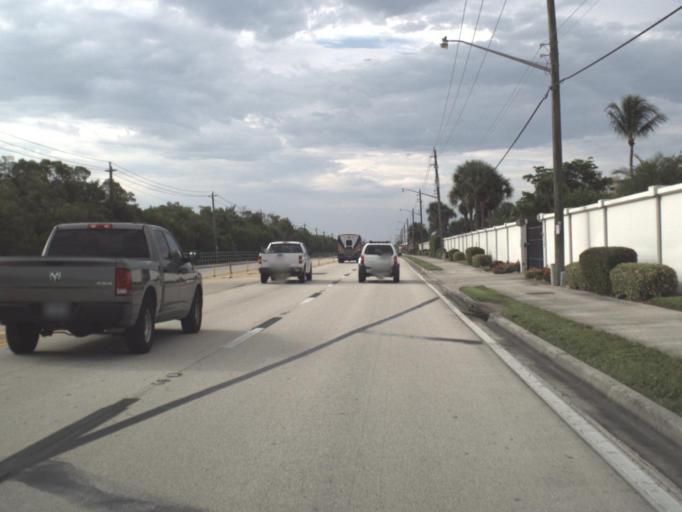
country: US
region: Florida
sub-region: Lee County
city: Fort Myers Beach
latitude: 26.4753
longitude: -81.9513
